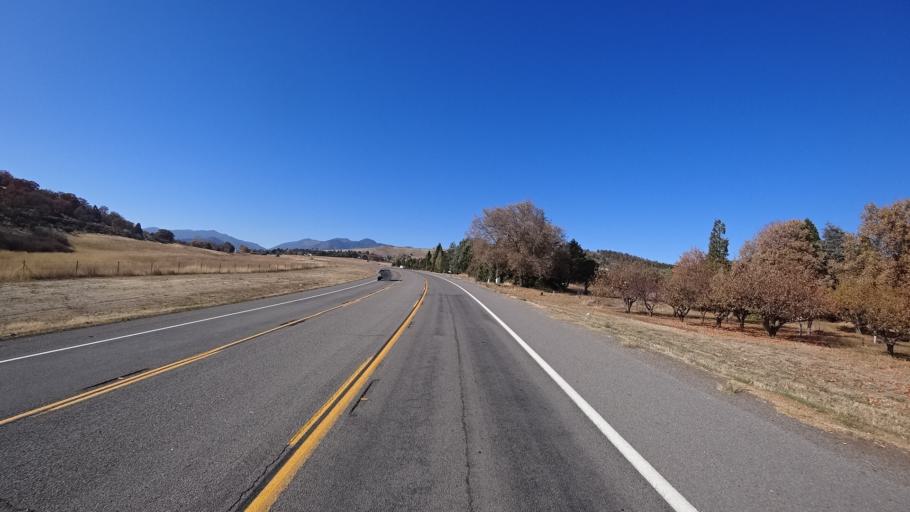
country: US
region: California
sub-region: Siskiyou County
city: Yreka
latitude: 41.7420
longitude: -122.6010
